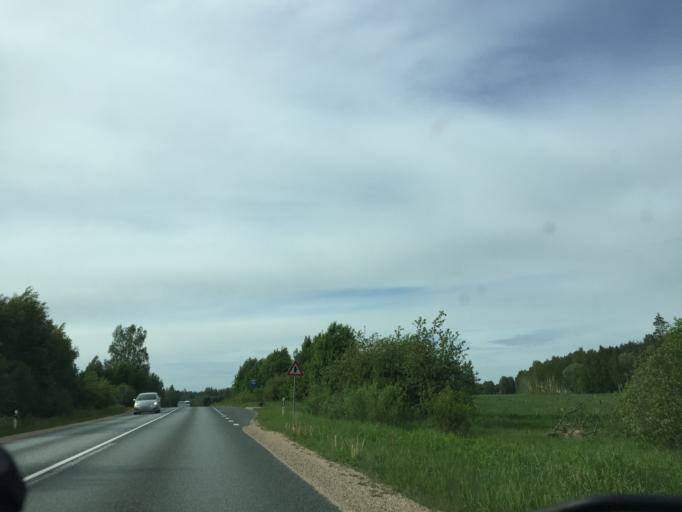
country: LV
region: Beverina
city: Murmuiza
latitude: 57.4595
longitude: 25.4183
